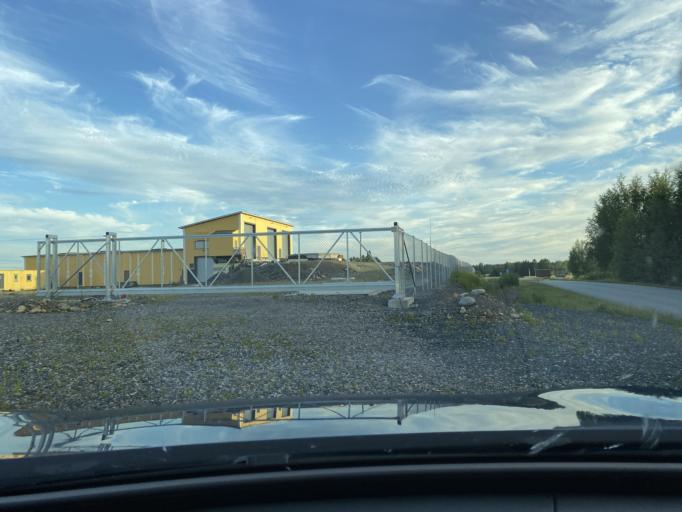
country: FI
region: Pirkanmaa
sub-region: Lounais-Pirkanmaa
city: Punkalaidun
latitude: 61.0408
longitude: 23.0000
